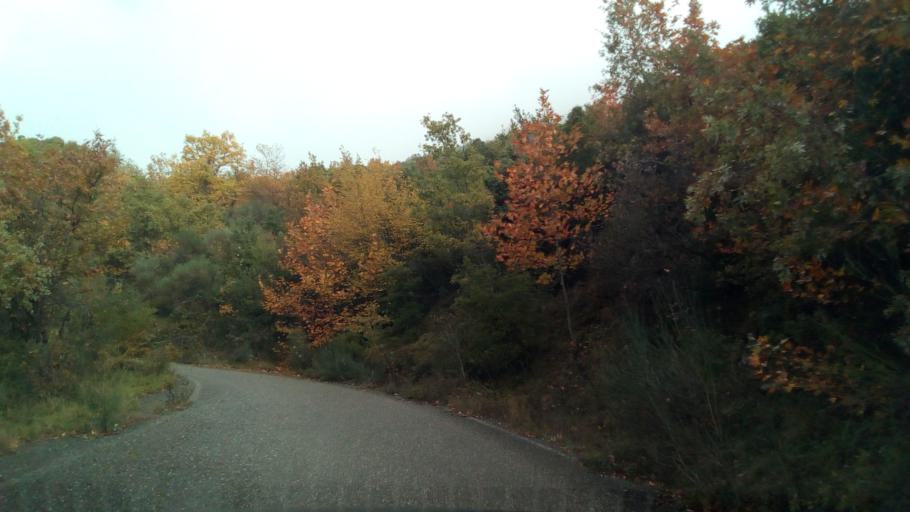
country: GR
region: West Greece
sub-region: Nomos Aitolias kai Akarnanias
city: Nafpaktos
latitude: 38.5180
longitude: 21.9522
